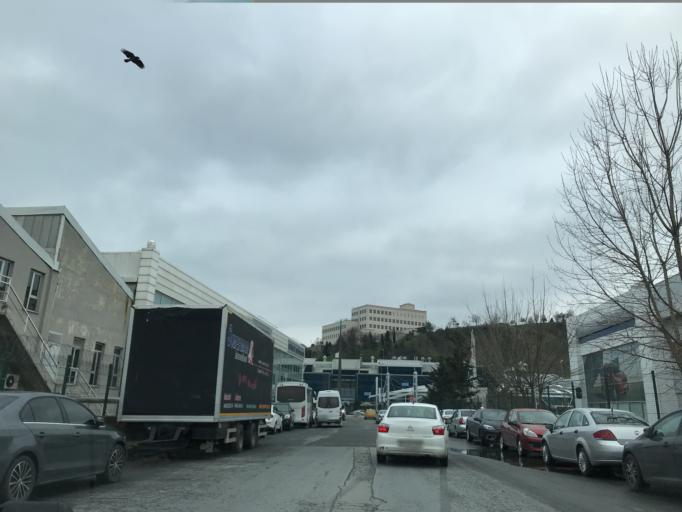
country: TR
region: Istanbul
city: Sisli
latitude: 41.1214
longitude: 29.0481
